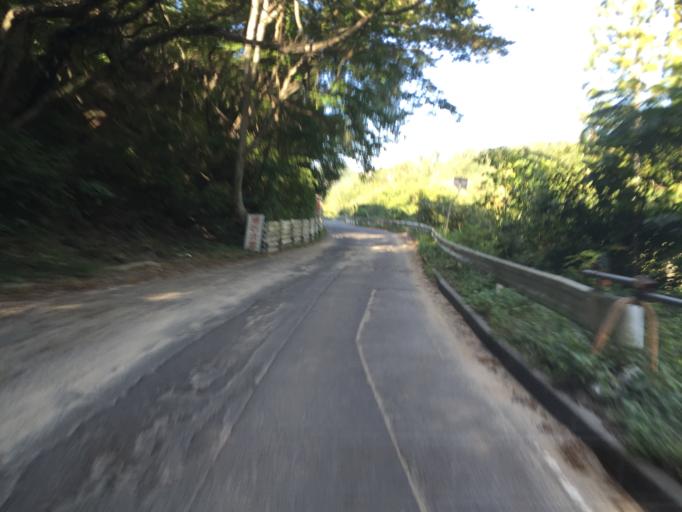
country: JP
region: Miyagi
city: Marumori
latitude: 37.8658
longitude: 140.7789
